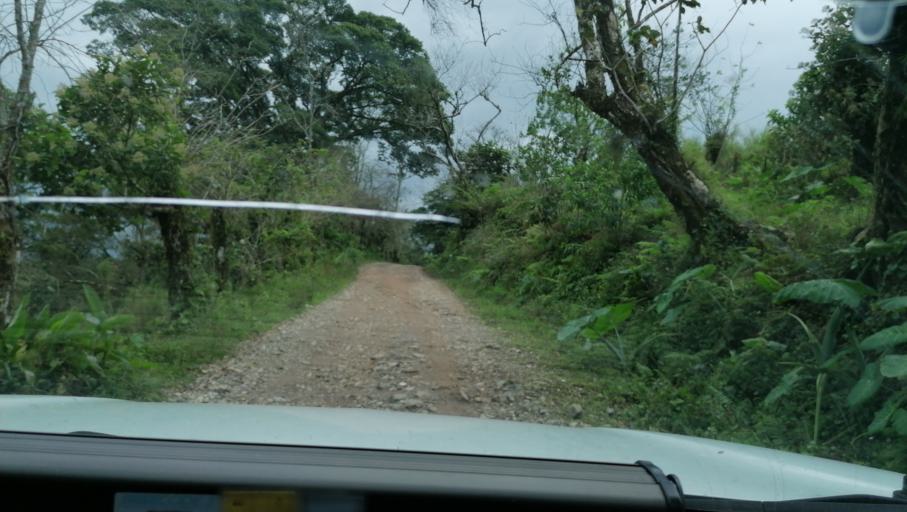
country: MX
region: Chiapas
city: Ixtacomitan
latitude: 17.3487
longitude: -93.1421
